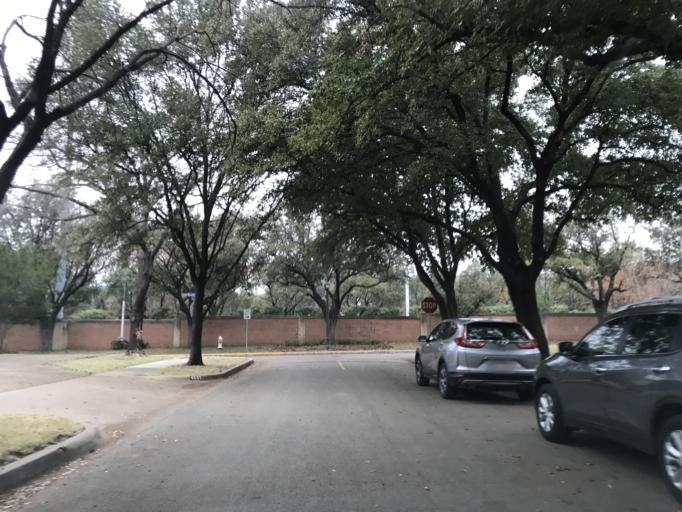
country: US
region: Texas
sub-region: Dallas County
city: Highland Park
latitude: 32.8250
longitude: -96.8157
